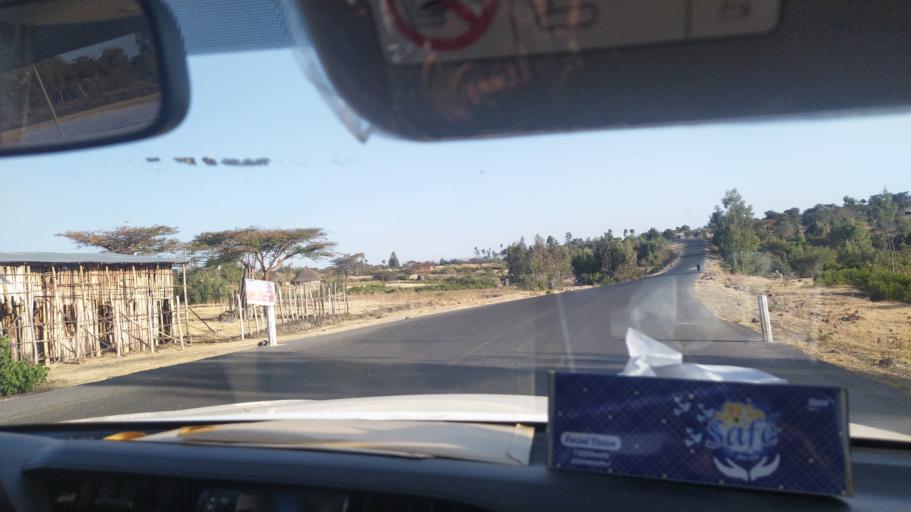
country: ET
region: Southern Nations, Nationalities, and People's Region
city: K'olito
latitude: 7.6997
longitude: 38.1300
